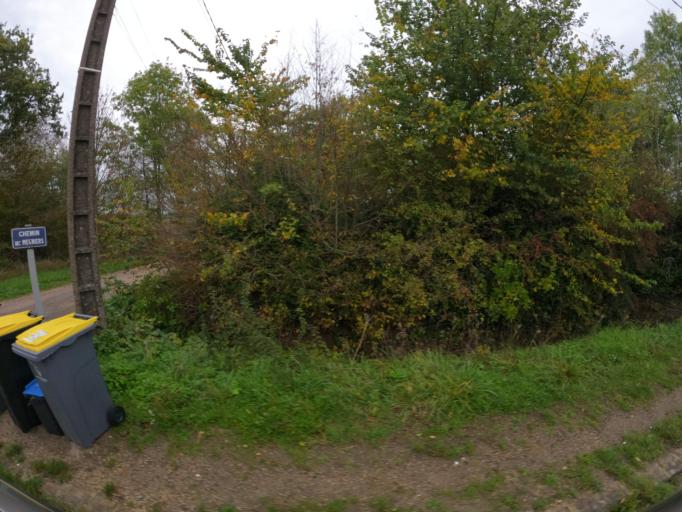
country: FR
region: Ile-de-France
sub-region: Departement de Seine-et-Marne
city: Villeneuve-le-Comte
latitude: 48.8195
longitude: 2.8313
